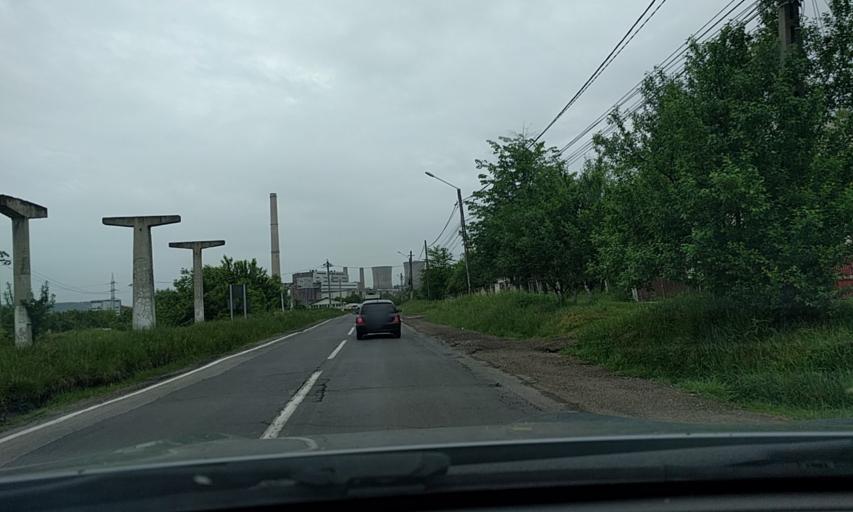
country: RO
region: Dambovita
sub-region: Comuna Doicesti
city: Doicesti
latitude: 44.9934
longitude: 25.4057
